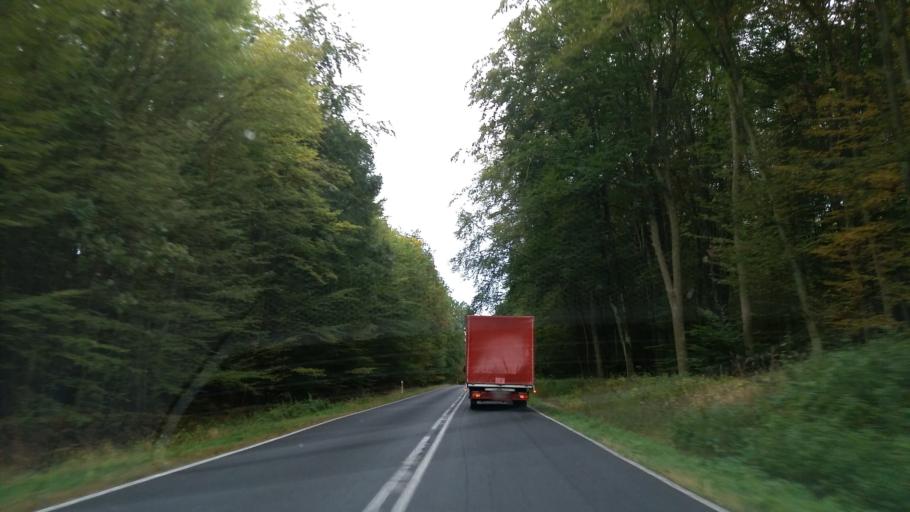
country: PL
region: West Pomeranian Voivodeship
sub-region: Powiat mysliborski
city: Barlinek
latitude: 52.9318
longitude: 15.1938
